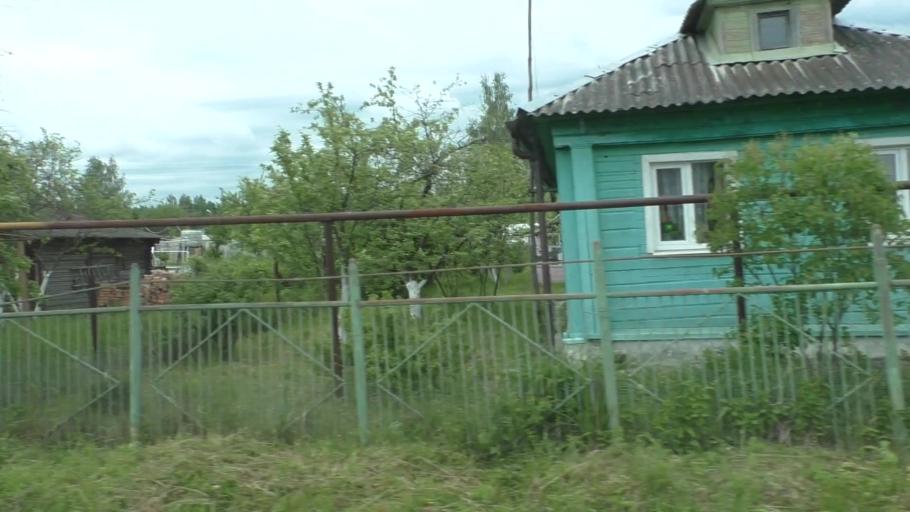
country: RU
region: Moskovskaya
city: Il'inskiy Pogost
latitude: 55.4694
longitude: 38.8970
